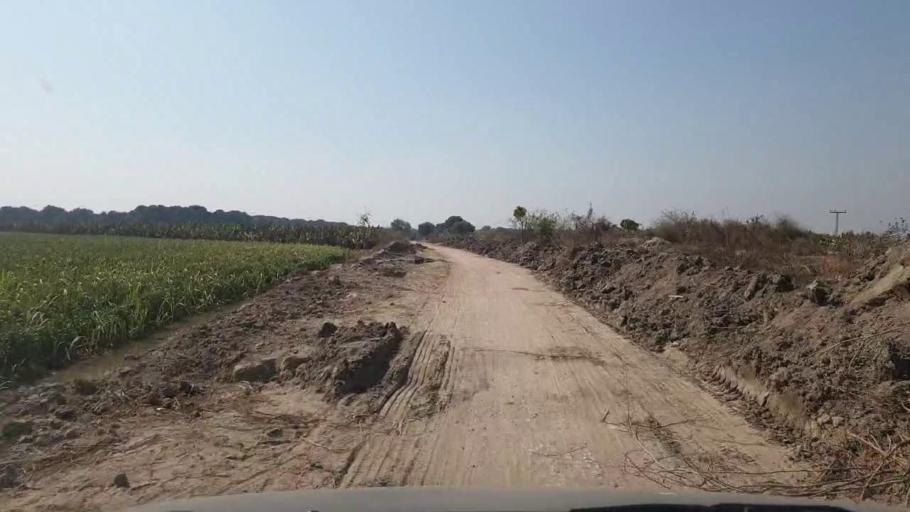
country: PK
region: Sindh
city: Tando Jam
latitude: 25.4235
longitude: 68.6293
